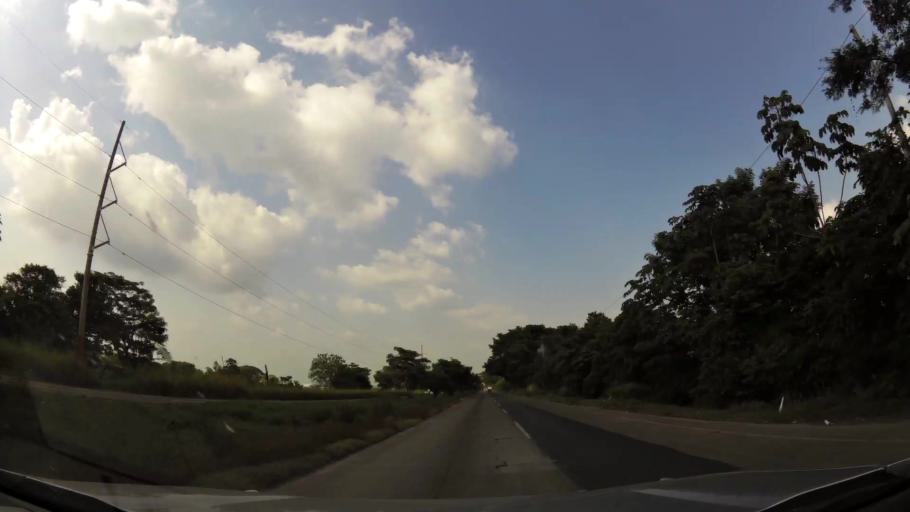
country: GT
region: Escuintla
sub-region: Municipio de Masagua
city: Masagua
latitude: 14.0798
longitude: -90.7779
